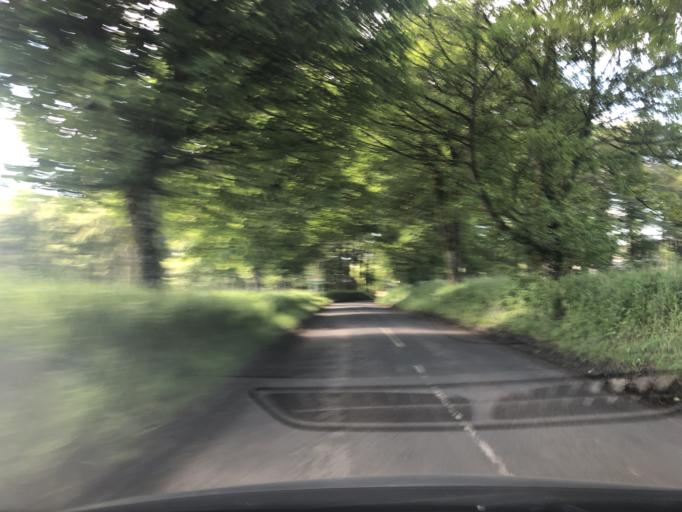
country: GB
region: Scotland
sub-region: Angus
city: Kirriemuir
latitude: 56.7314
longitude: -3.0044
